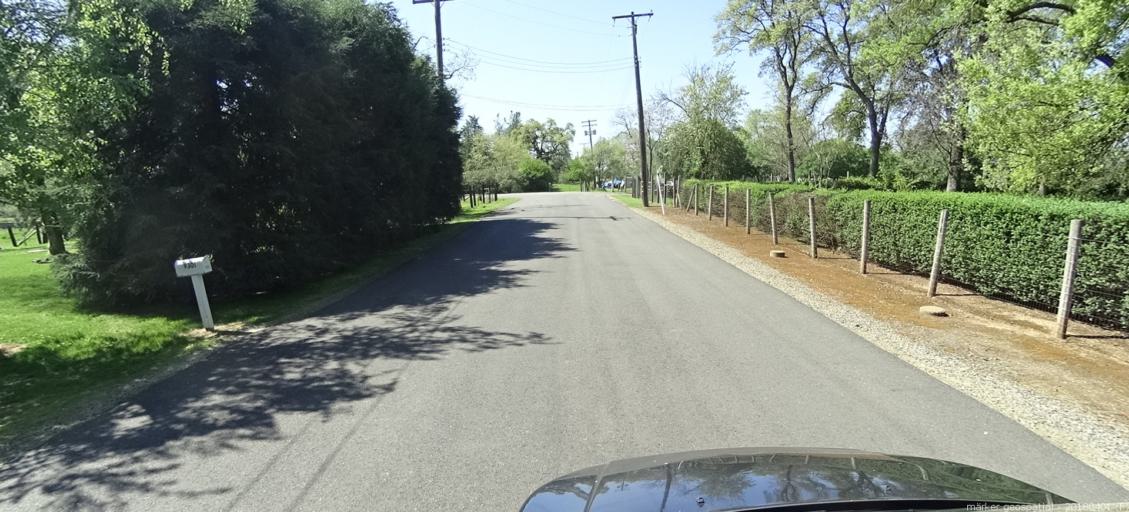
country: US
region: California
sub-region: Sacramento County
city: Wilton
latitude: 38.4141
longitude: -121.2704
